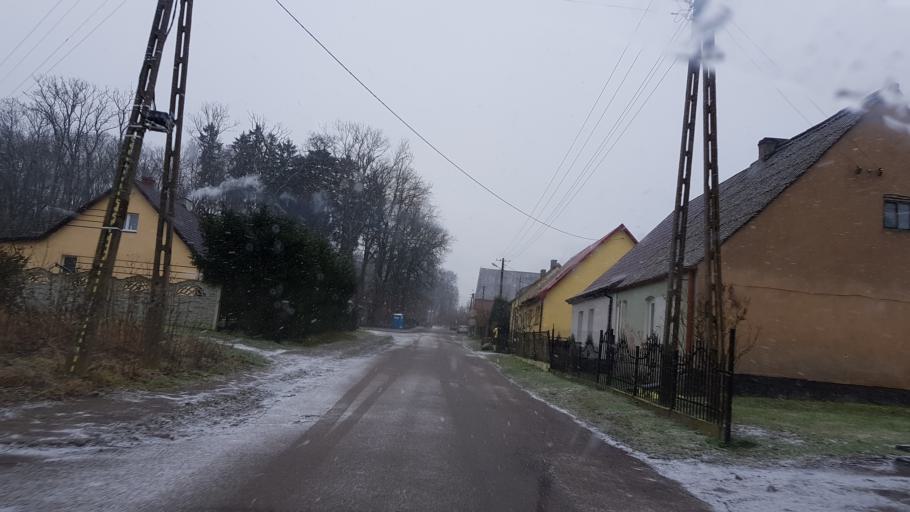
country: PL
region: West Pomeranian Voivodeship
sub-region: Powiat slawienski
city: Slawno
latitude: 54.2826
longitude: 16.6002
